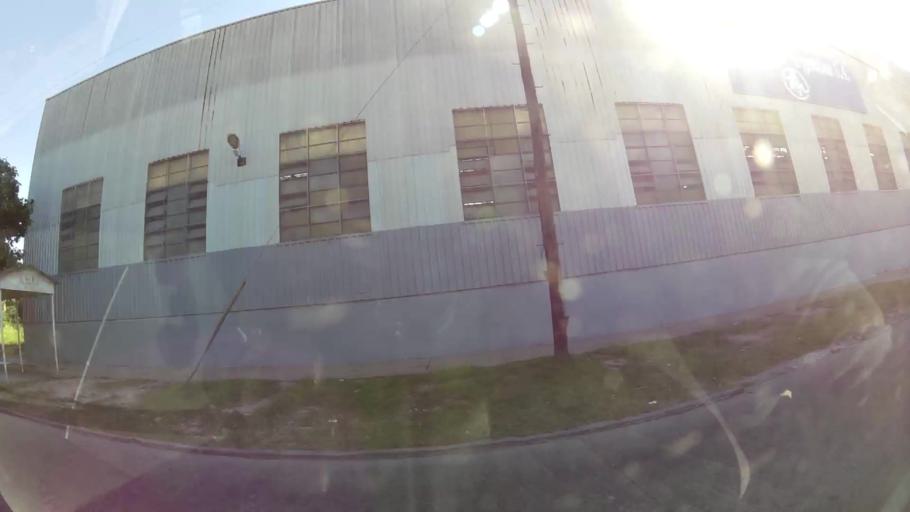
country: AR
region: Buenos Aires
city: Hurlingham
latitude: -34.5582
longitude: -58.6043
